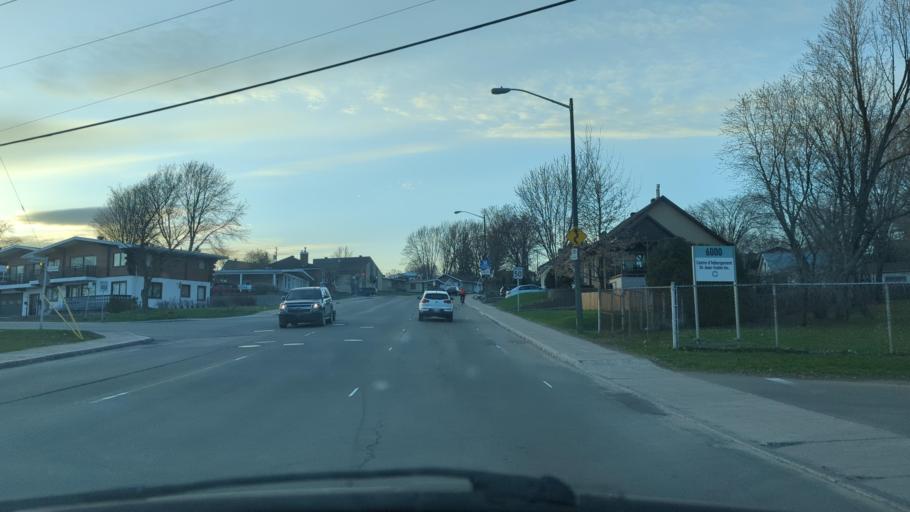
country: CA
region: Quebec
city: Quebec
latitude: 46.8497
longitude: -71.2615
